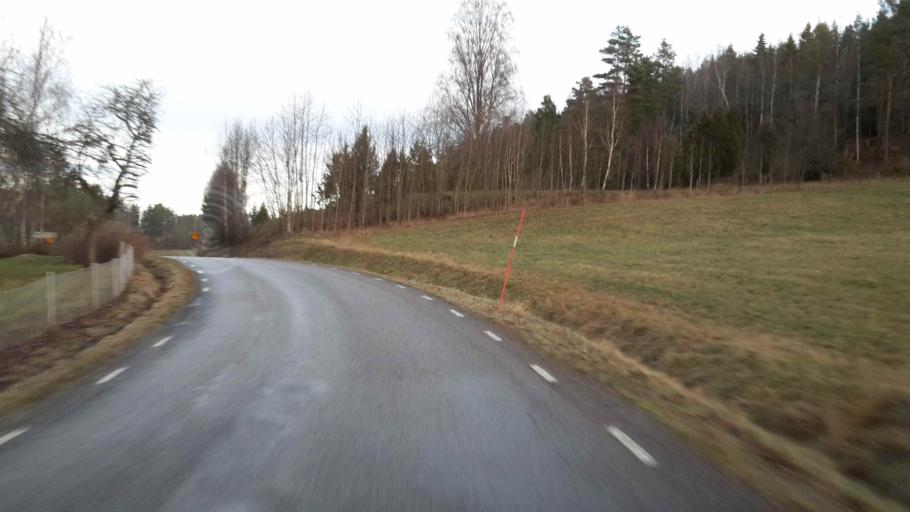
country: SE
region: Kalmar
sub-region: Vasterviks Kommun
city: Overum
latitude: 58.1604
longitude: 16.3316
